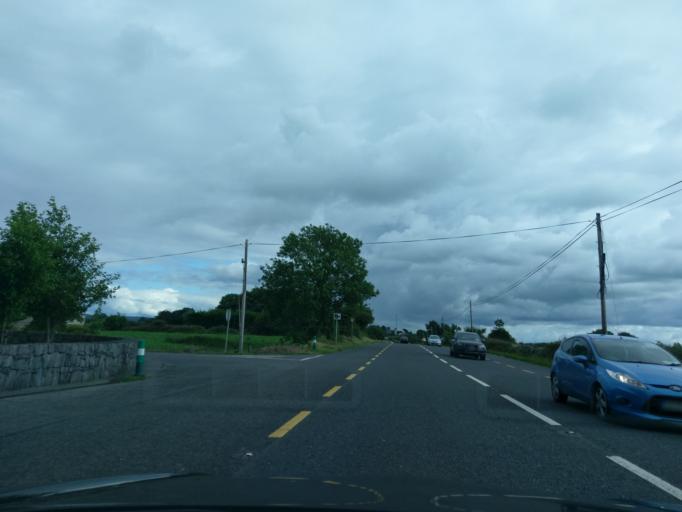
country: IE
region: Connaught
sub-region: County Galway
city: Gort
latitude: 53.1643
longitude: -8.8148
